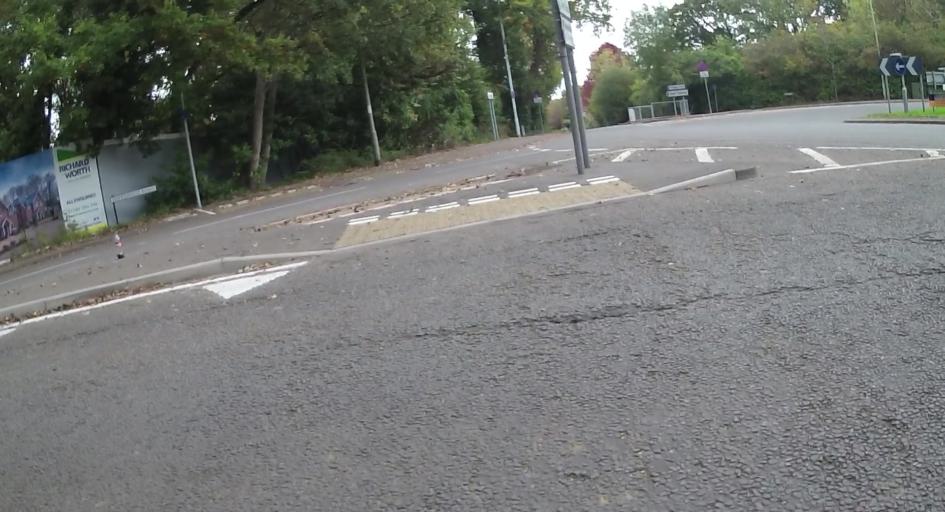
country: GB
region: England
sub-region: Bracknell Forest
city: Binfield
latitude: 51.4215
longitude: -0.7796
